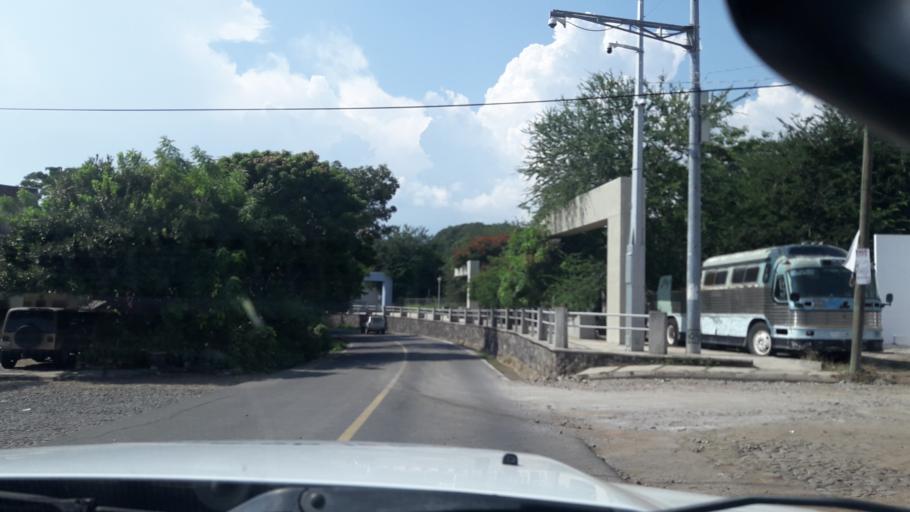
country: MX
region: Colima
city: Comala
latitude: 19.3318
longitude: -103.7516
